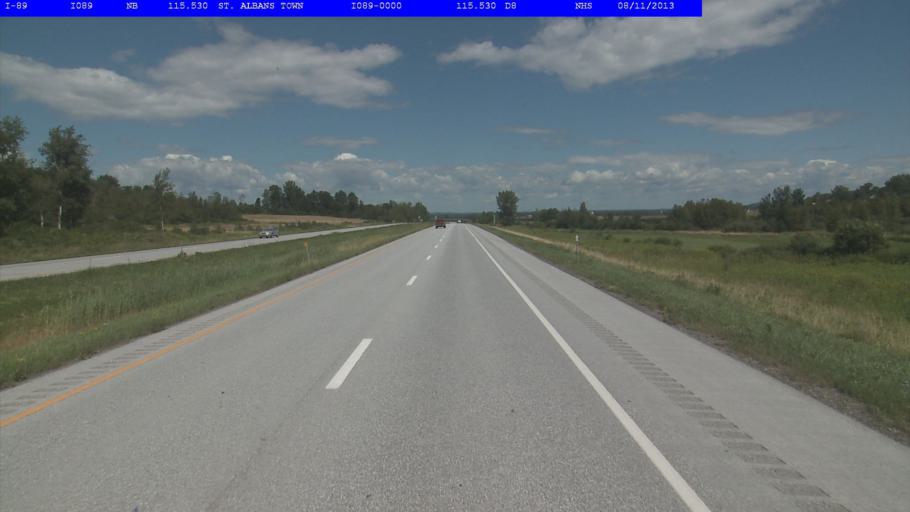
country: US
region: Vermont
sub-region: Franklin County
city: Saint Albans
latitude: 44.8200
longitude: -73.0628
